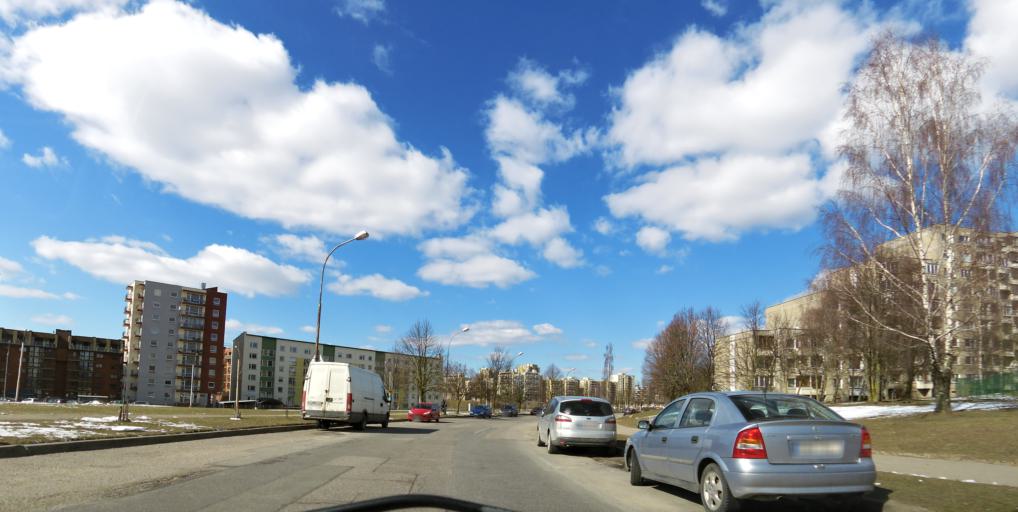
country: LT
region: Vilnius County
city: Pasilaiciai
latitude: 54.7317
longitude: 25.2217
